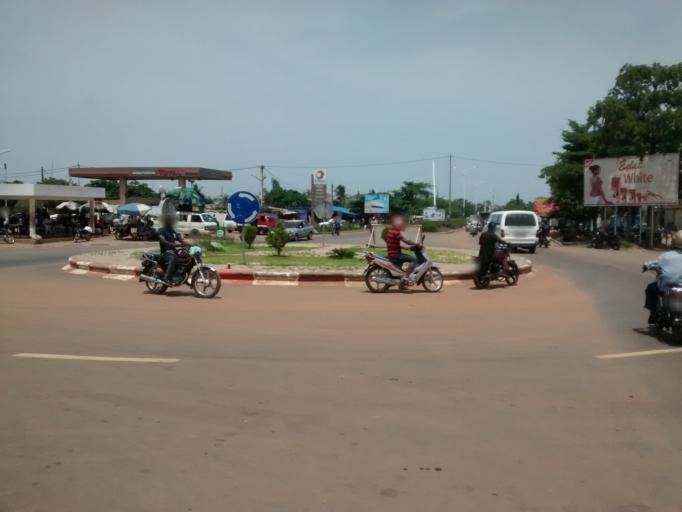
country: TG
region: Maritime
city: Lome
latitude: 6.1982
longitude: 1.2001
